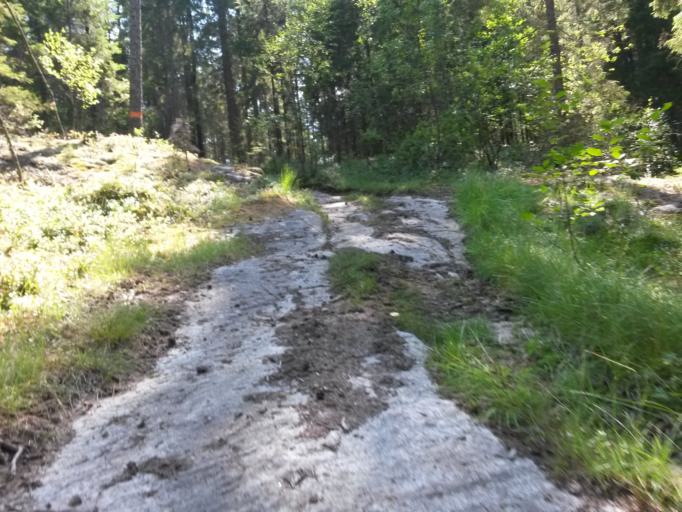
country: SE
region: Vaestra Goetaland
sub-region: Vargarda Kommun
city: Jonstorp
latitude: 57.9568
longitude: 12.6838
